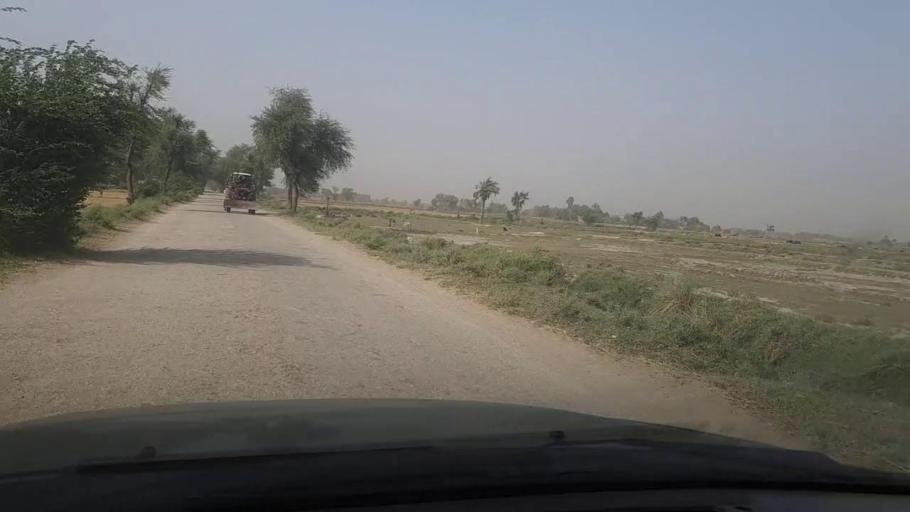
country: PK
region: Sindh
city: Shikarpur
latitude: 27.9262
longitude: 68.6147
